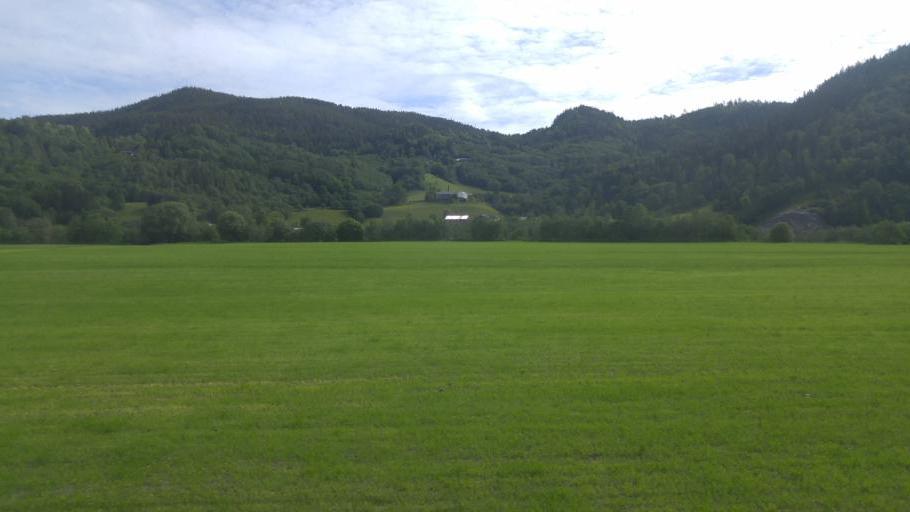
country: NO
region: Sor-Trondelag
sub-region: Midtre Gauldal
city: Storen
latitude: 63.0885
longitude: 10.2416
